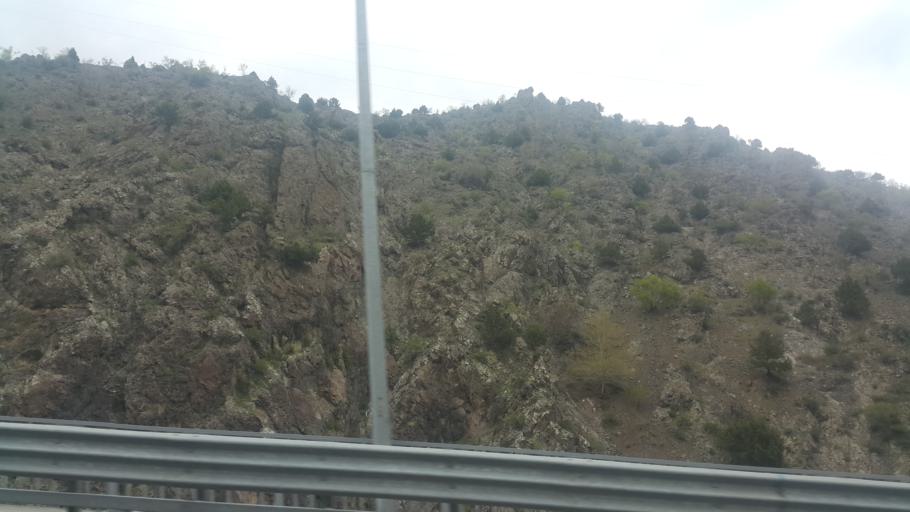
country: TR
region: Nigde
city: Ciftehan
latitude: 37.5553
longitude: 34.7701
